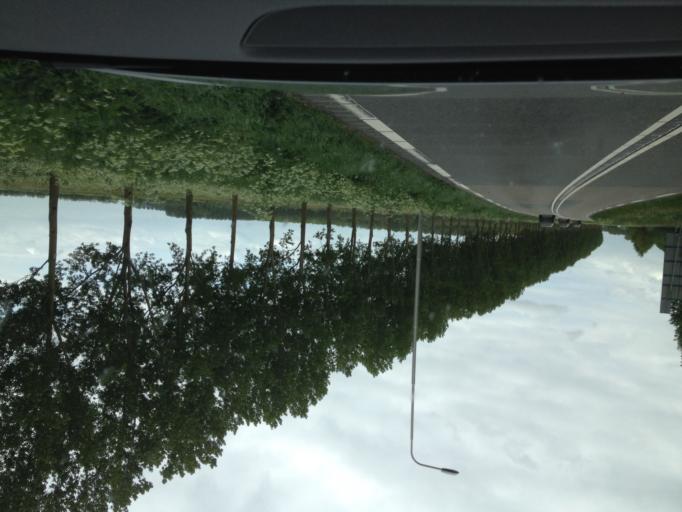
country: NL
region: North Holland
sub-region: Gemeente Huizen
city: Huizen
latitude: 52.3355
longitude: 5.2715
